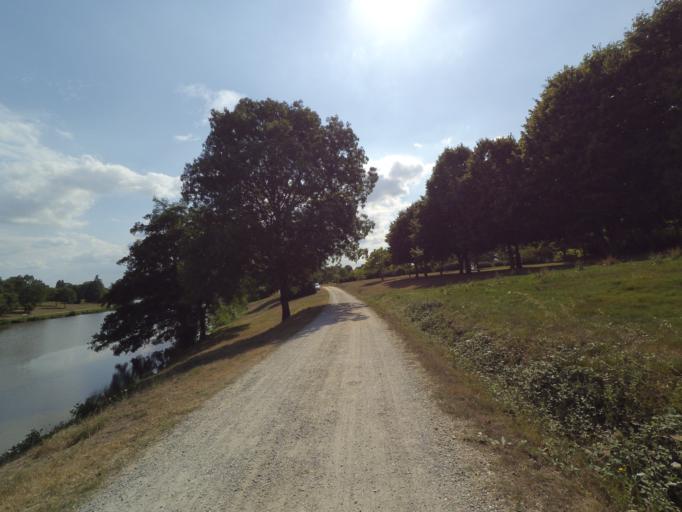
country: FR
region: Pays de la Loire
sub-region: Departement de la Loire-Atlantique
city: Vieillevigne
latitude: 46.9656
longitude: -1.4329
